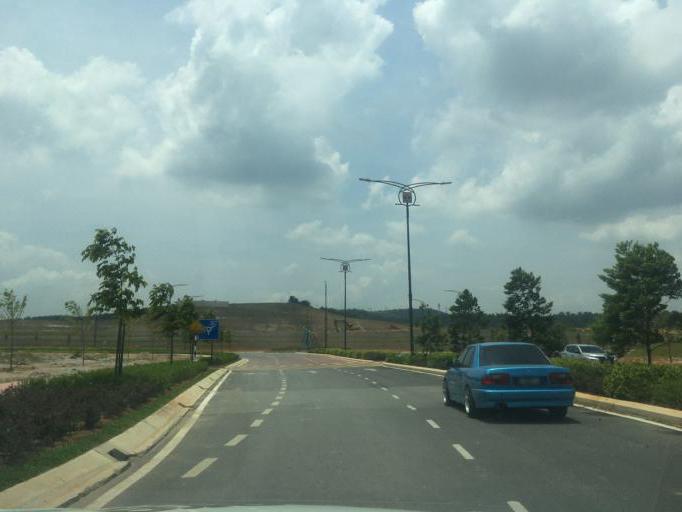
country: MY
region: Putrajaya
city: Putrajaya
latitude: 2.8452
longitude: 101.7054
